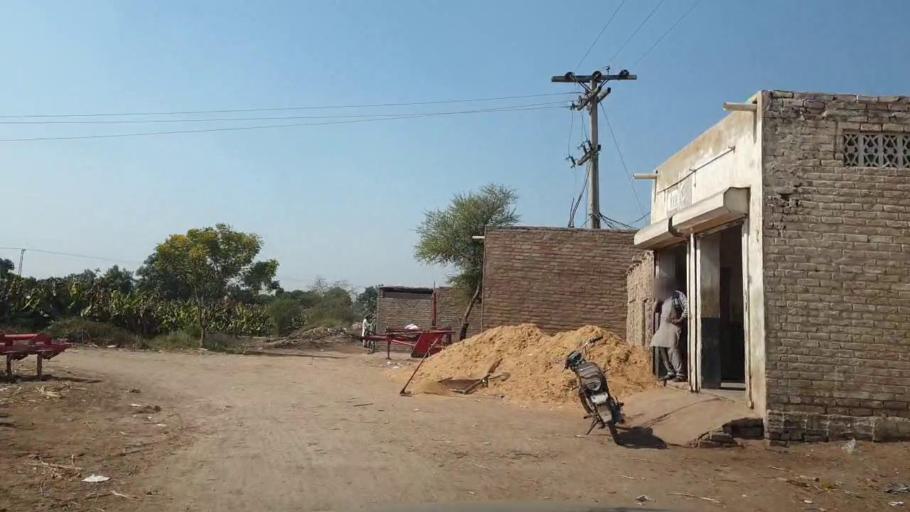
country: PK
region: Sindh
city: Tando Allahyar
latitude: 25.5471
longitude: 68.6793
